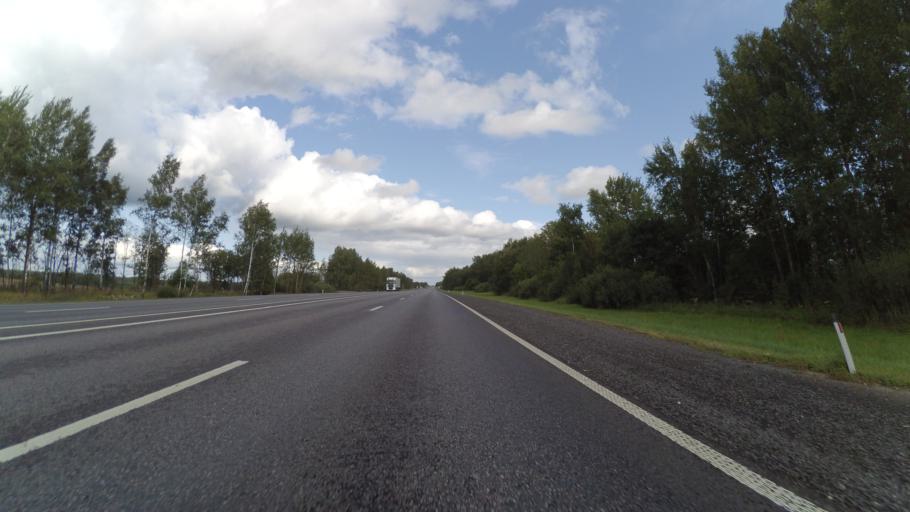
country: RU
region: Smolensk
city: Pechersk
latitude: 54.8613
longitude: 31.9203
